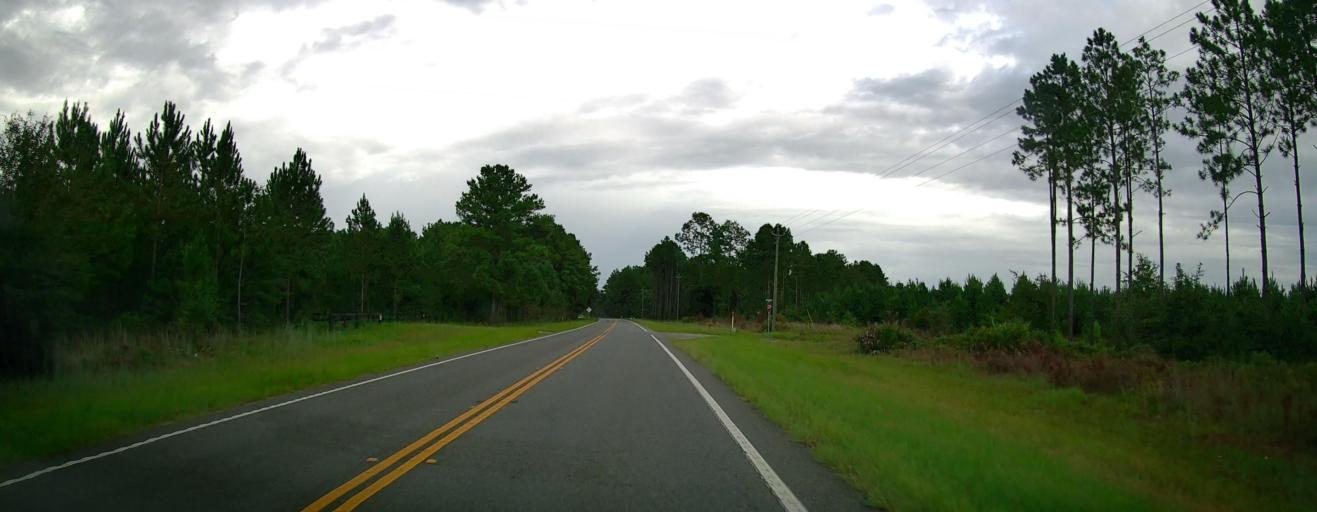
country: US
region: Georgia
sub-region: Ware County
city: Deenwood
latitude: 31.2854
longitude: -82.5479
